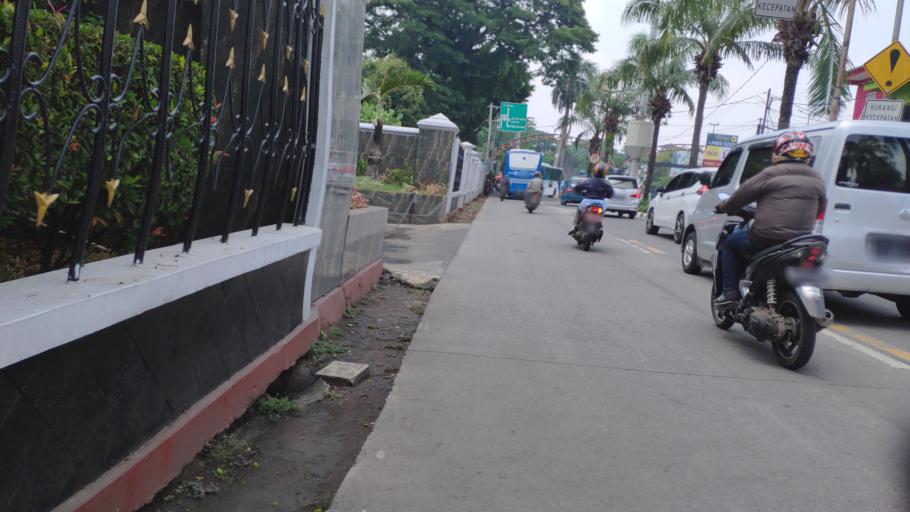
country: ID
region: West Java
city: Pamulang
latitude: -6.3051
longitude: 106.8208
